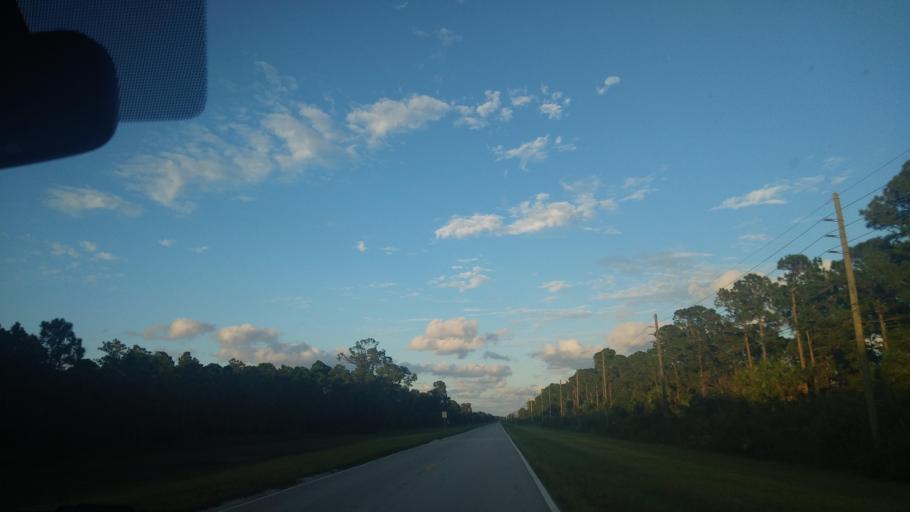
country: US
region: Florida
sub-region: Indian River County
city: Fellsmere
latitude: 27.7521
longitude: -80.6254
